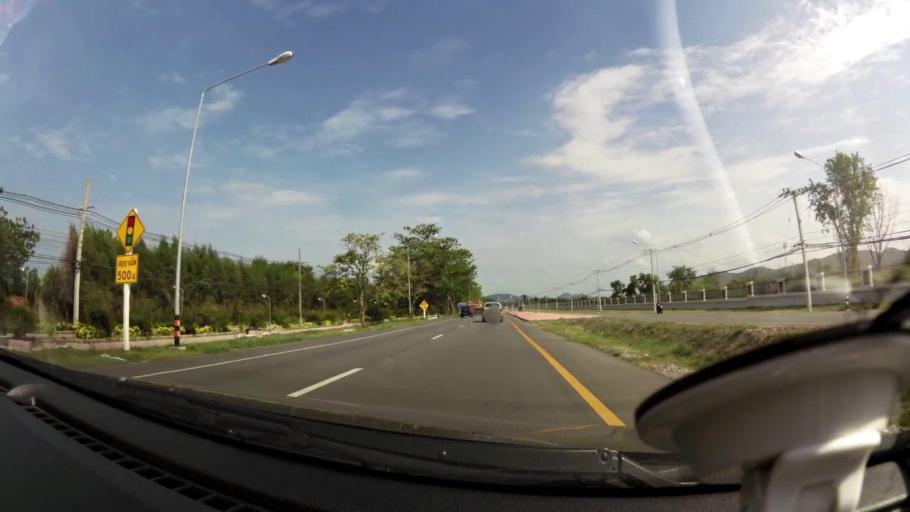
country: TH
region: Prachuap Khiri Khan
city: Hua Hin
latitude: 12.5056
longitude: 99.9678
